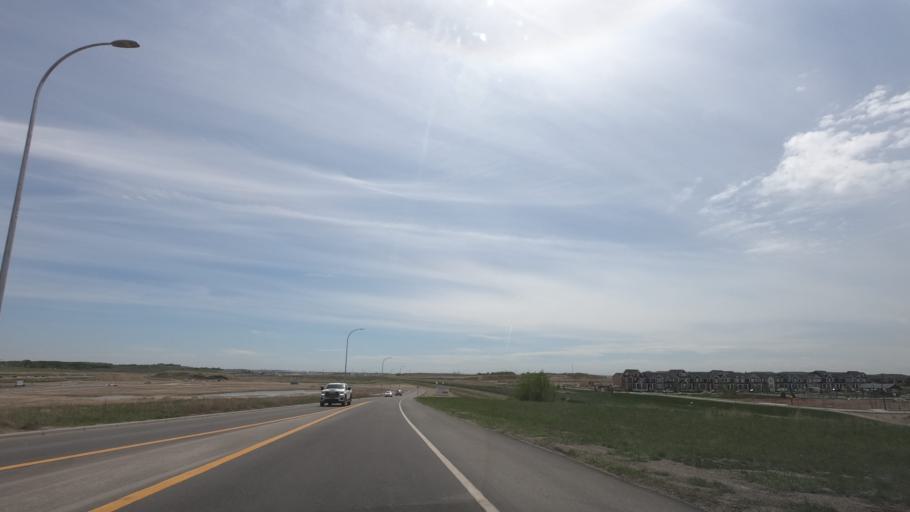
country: CA
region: Alberta
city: Airdrie
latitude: 51.2557
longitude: -114.0073
